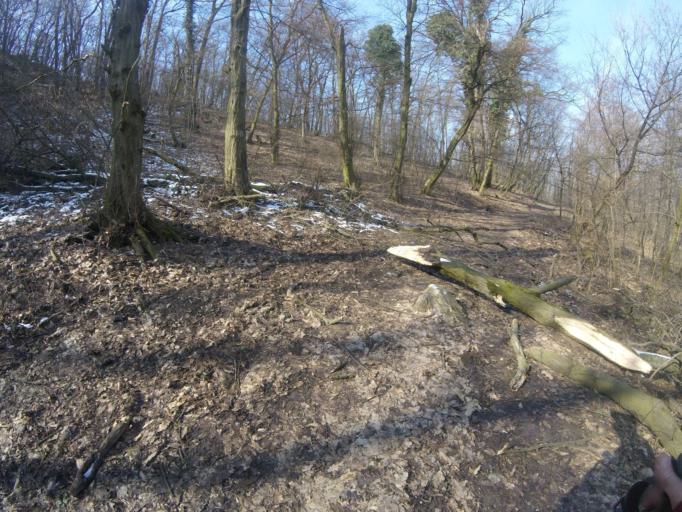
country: HU
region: Komarom-Esztergom
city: Nyergesujfalu
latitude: 47.7399
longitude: 18.5523
